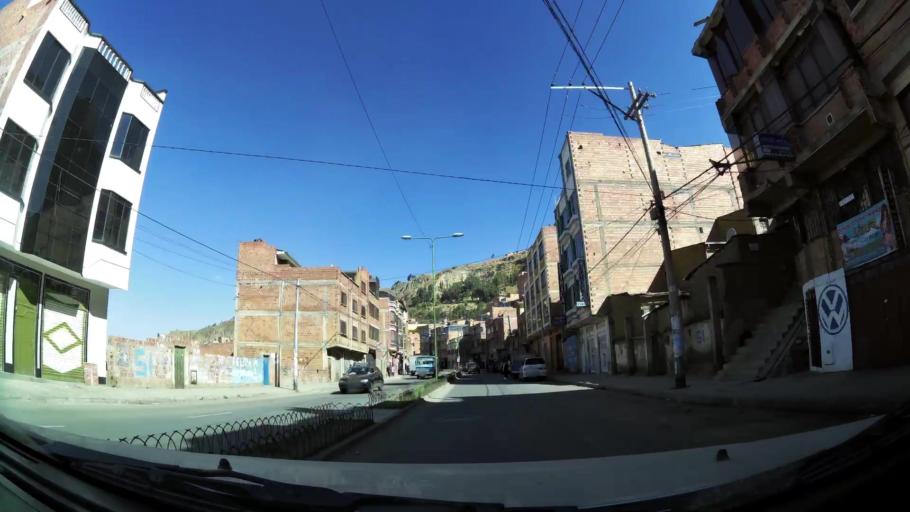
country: BO
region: La Paz
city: La Paz
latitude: -16.5132
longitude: -68.1441
